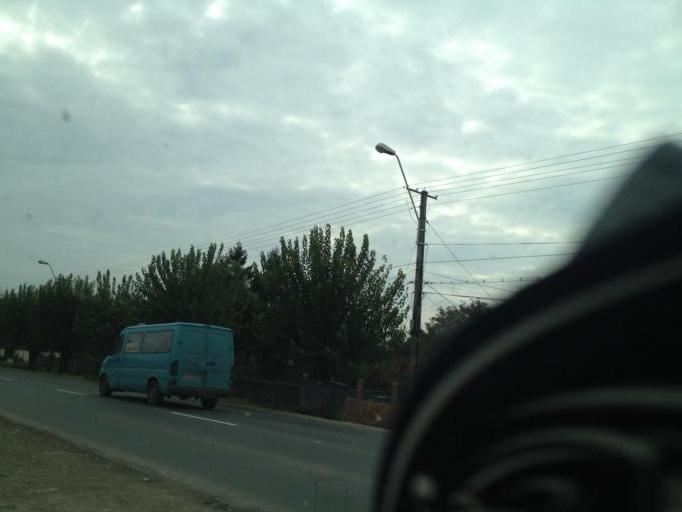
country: RO
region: Dolj
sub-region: Municipiul Craiova
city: Facai
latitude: 44.2839
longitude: 23.8026
